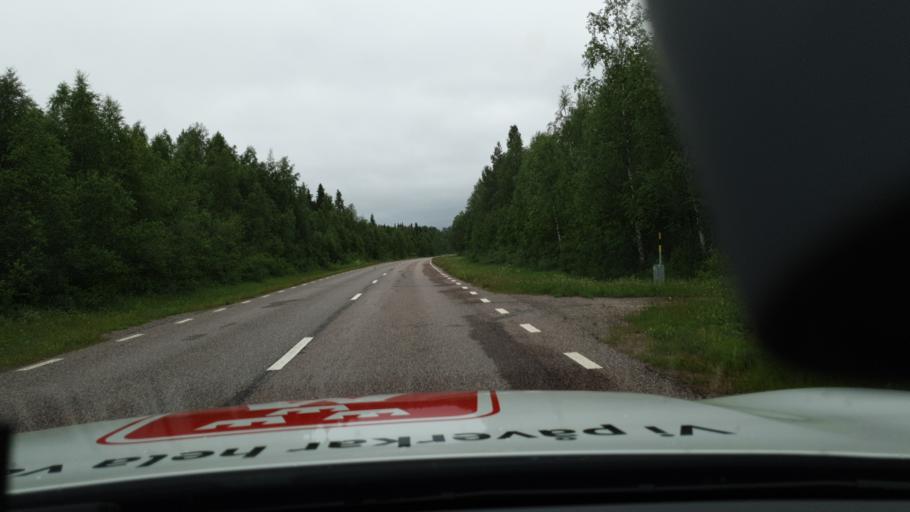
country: FI
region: Lapland
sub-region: Tunturi-Lappi
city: Kolari
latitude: 67.0702
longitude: 23.6626
